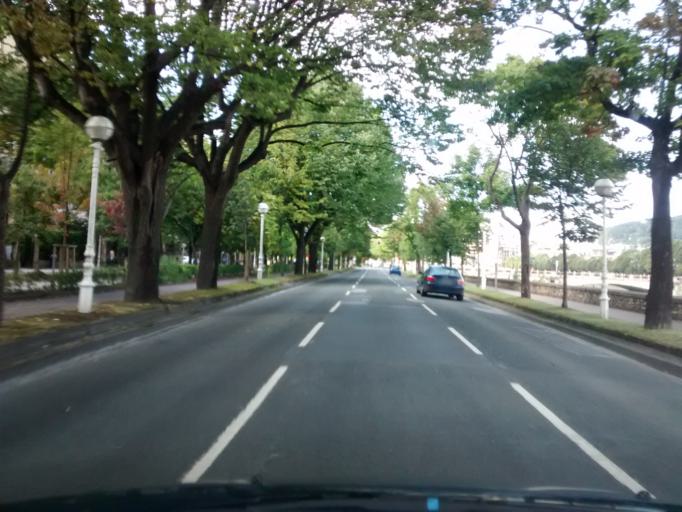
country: ES
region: Basque Country
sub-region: Provincia de Guipuzcoa
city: San Sebastian
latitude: 43.3159
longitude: -1.9791
